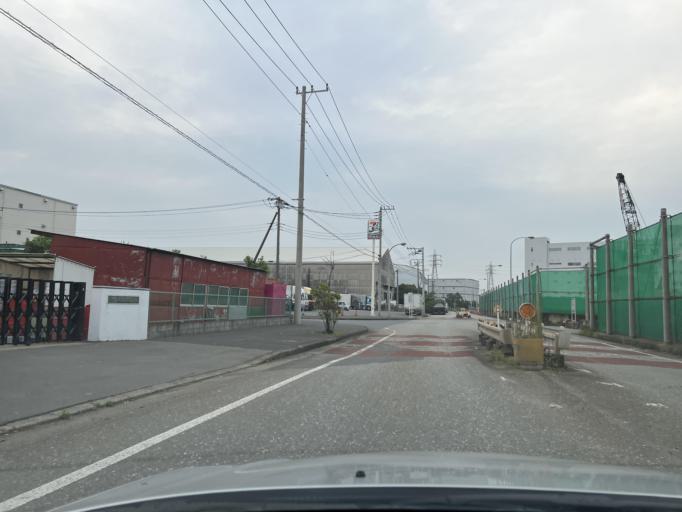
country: JP
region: Chiba
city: Funabashi
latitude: 35.6754
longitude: 139.9708
